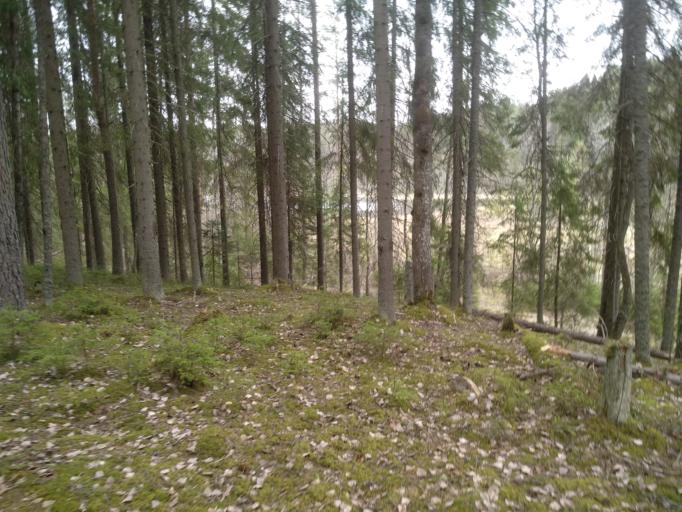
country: RU
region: Leningrad
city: Sosnovo
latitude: 60.4806
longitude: 30.1564
